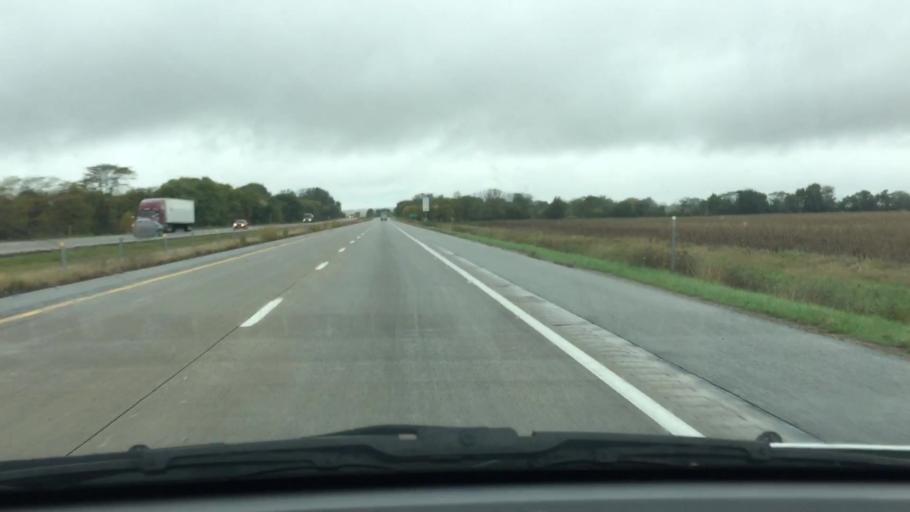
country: US
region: Iowa
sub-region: Jasper County
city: Colfax
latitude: 41.6944
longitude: -93.1895
